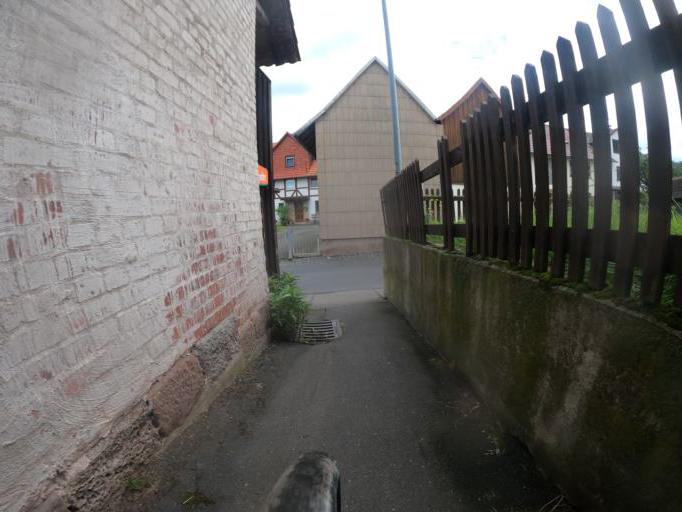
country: DE
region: Thuringia
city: Lindewerra
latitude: 51.3076
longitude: 9.9242
